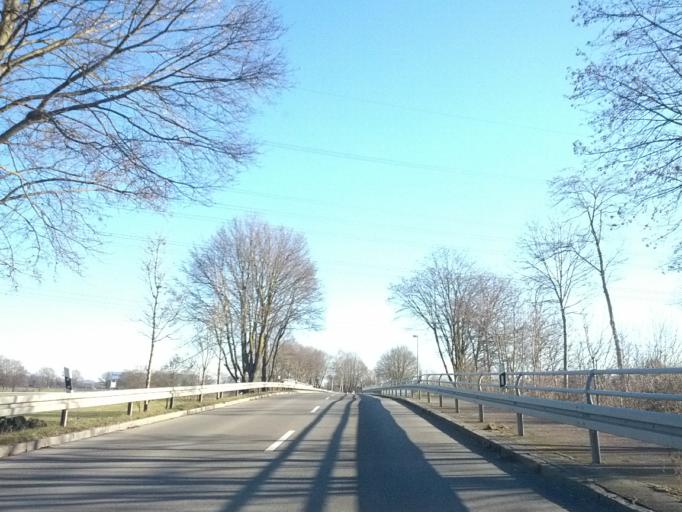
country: DE
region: Bavaria
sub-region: Swabia
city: Buxheim
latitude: 47.9930
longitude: 10.1446
